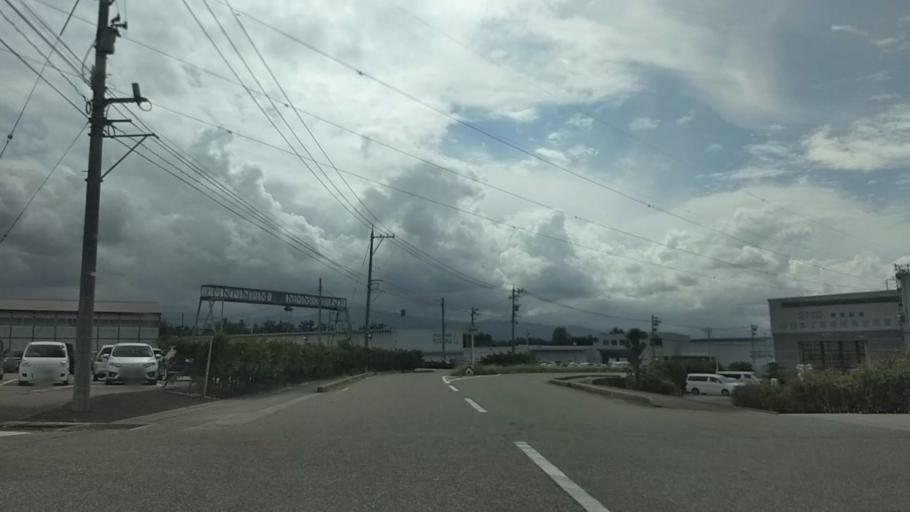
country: JP
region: Toyama
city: Kamiichi
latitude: 36.7421
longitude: 137.3770
